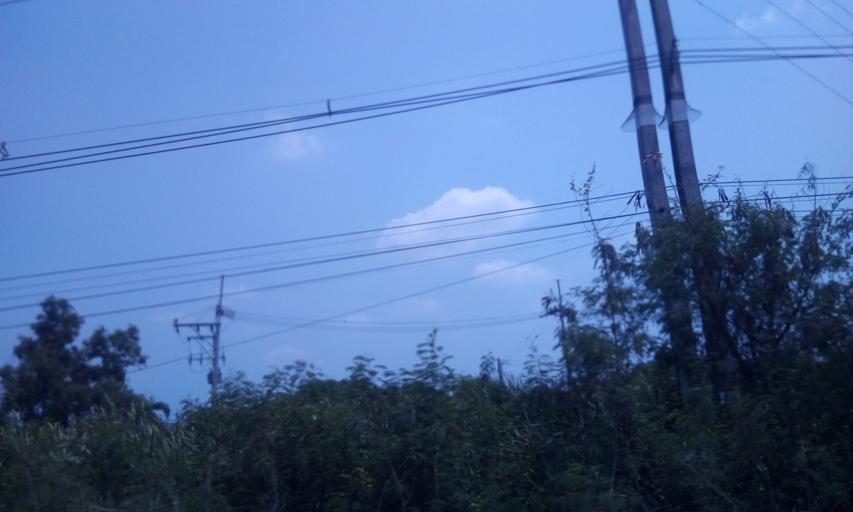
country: TH
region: Chachoengsao
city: Bang Nam Priao
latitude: 13.8429
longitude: 101.0523
